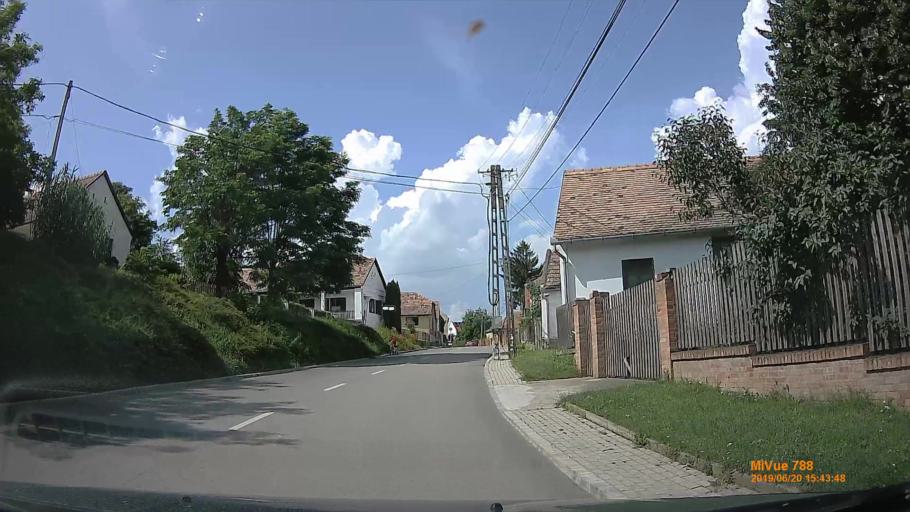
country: HU
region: Baranya
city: Kozarmisleny
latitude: 45.9832
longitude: 18.2609
